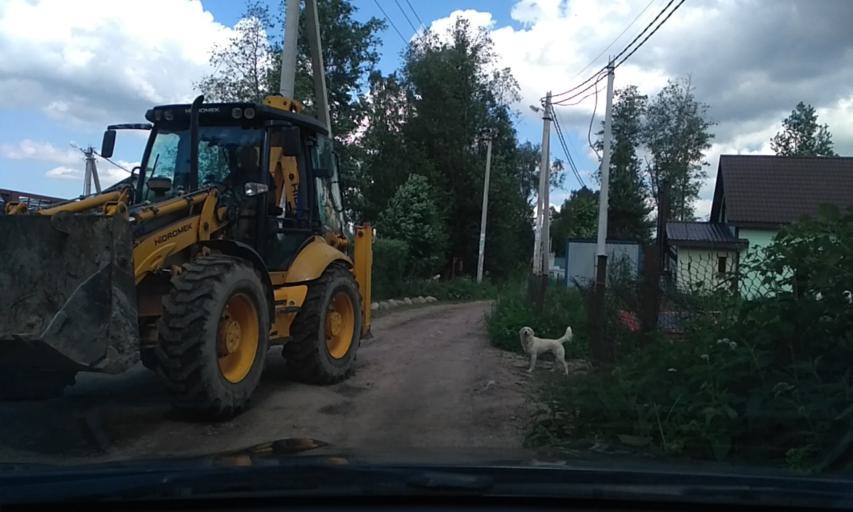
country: RU
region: Leningrad
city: Otradnoye
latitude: 59.8078
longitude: 30.8313
